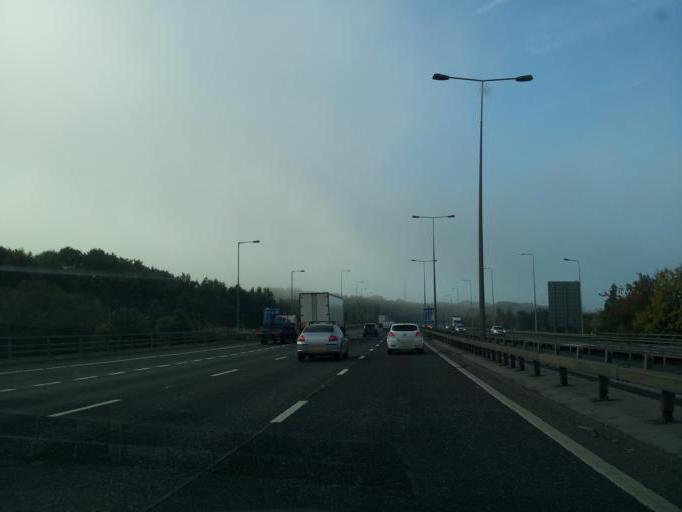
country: GB
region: England
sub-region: Calderdale
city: Brighouse
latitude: 53.6917
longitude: -1.7572
